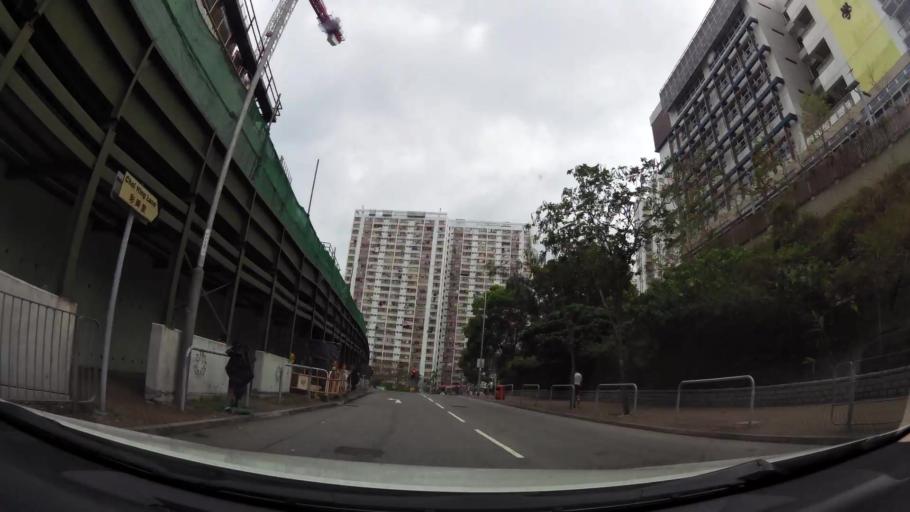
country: HK
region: Kowloon City
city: Kowloon
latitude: 22.3315
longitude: 114.2149
